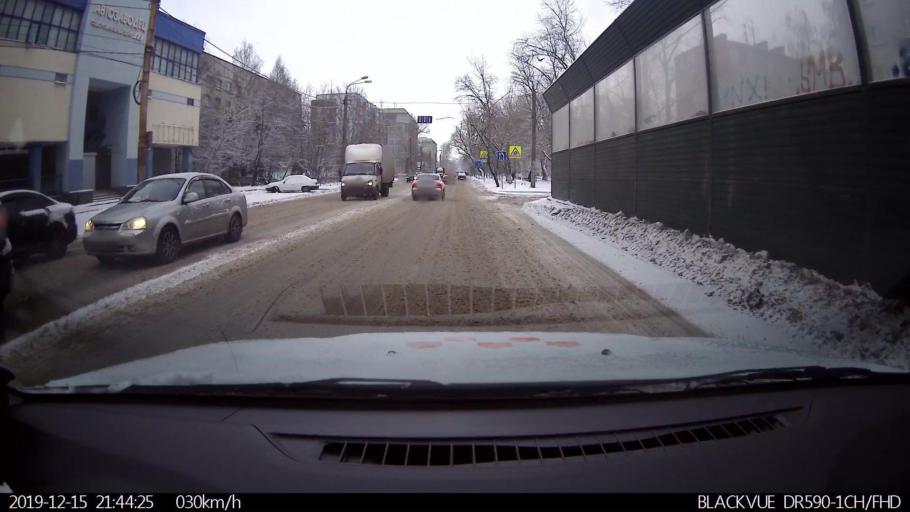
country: RU
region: Nizjnij Novgorod
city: Burevestnik
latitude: 56.2347
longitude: 43.8757
